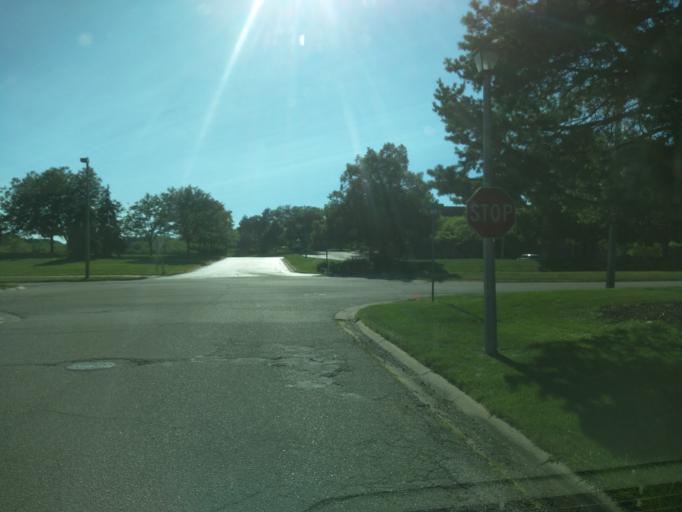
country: US
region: Michigan
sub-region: Eaton County
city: Waverly
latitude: 42.7254
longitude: -84.6367
